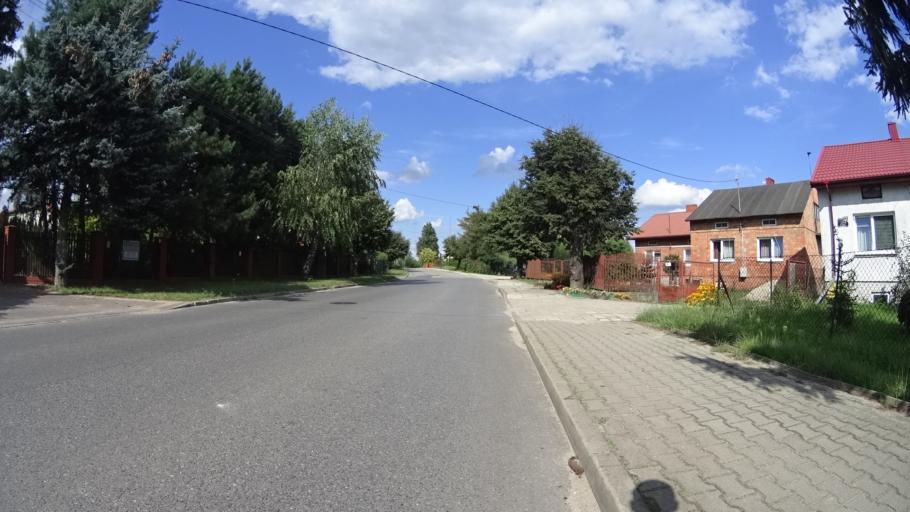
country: PL
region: Masovian Voivodeship
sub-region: Powiat grojecki
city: Mogielnica
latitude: 51.6844
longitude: 20.7170
